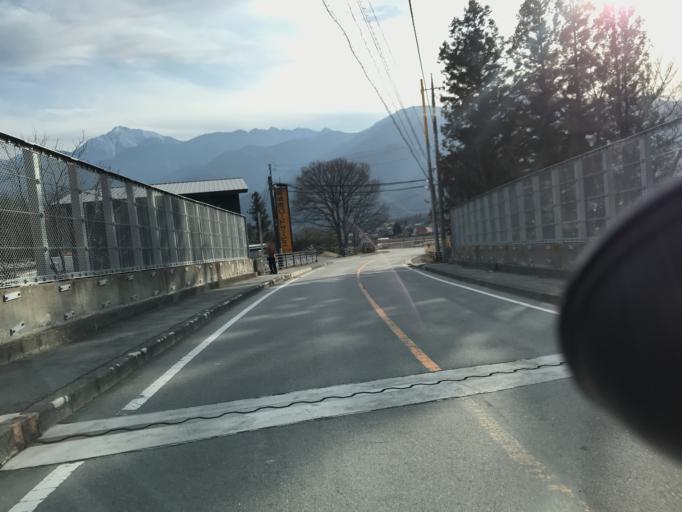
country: JP
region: Nagano
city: Chino
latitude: 35.8675
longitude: 138.3072
